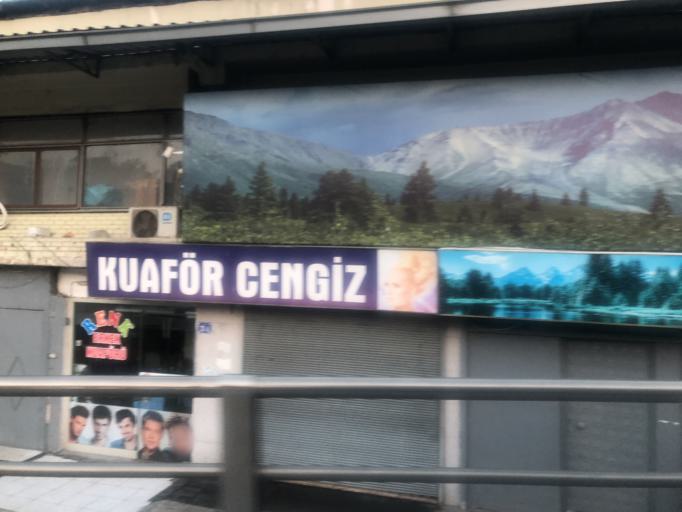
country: TR
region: Ankara
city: Ankara
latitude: 39.9501
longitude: 32.8575
